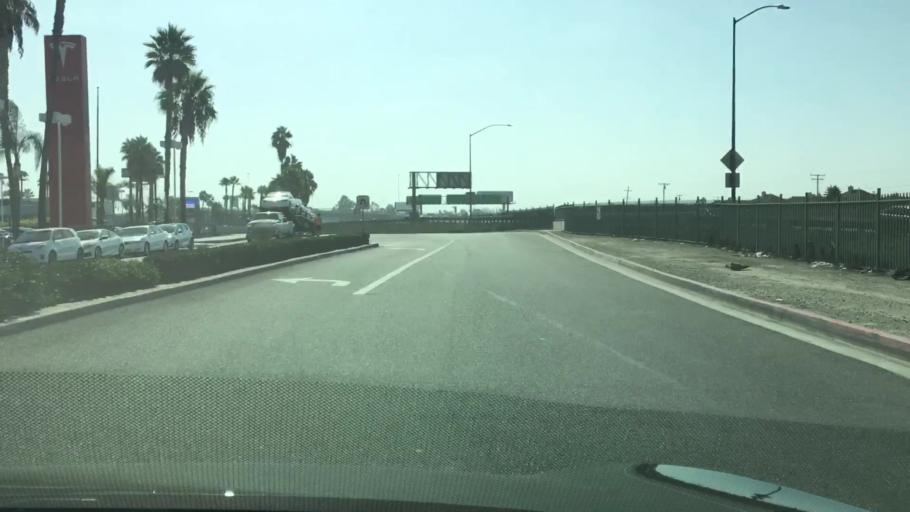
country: US
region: California
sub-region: Orange County
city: Buena Park
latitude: 33.8634
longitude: -117.9914
